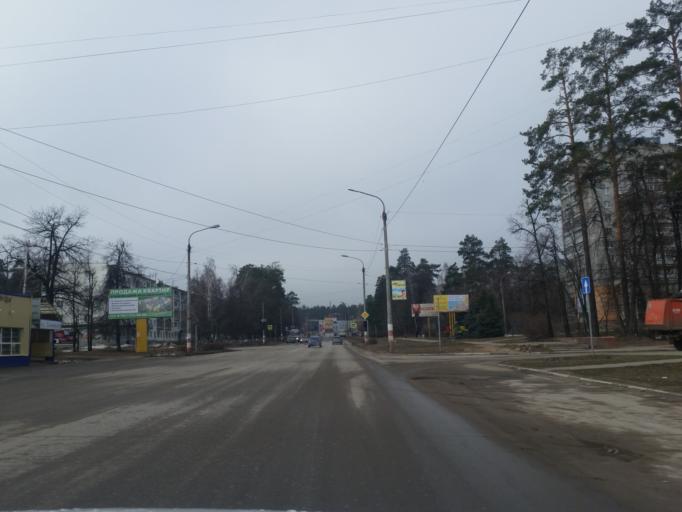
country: RU
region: Ulyanovsk
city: Dimitrovgrad
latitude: 54.2363
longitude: 49.5616
